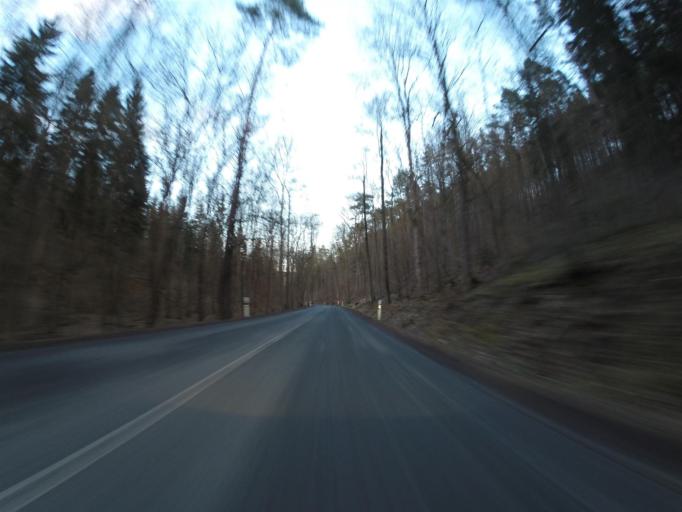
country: DE
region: Thuringia
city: Jena
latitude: 50.9355
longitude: 11.5414
